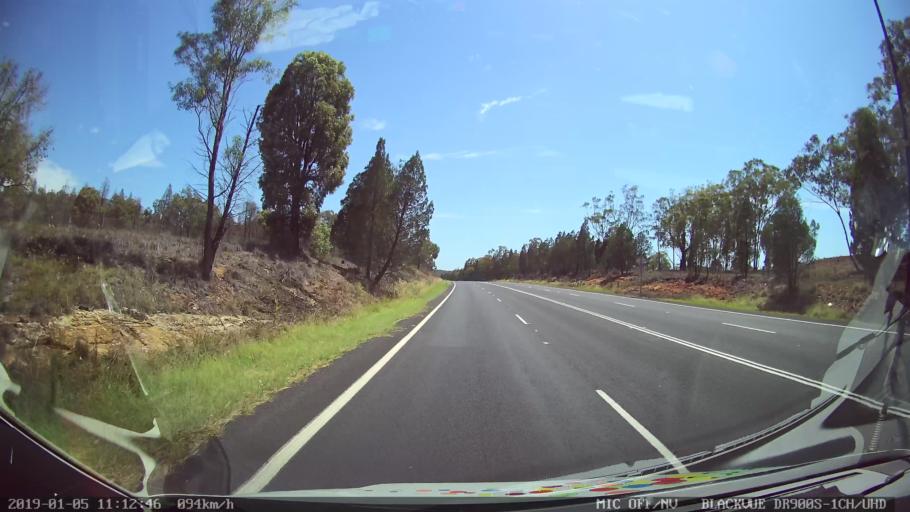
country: AU
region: New South Wales
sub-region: Warrumbungle Shire
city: Coonabarabran
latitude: -31.3786
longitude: 149.2644
